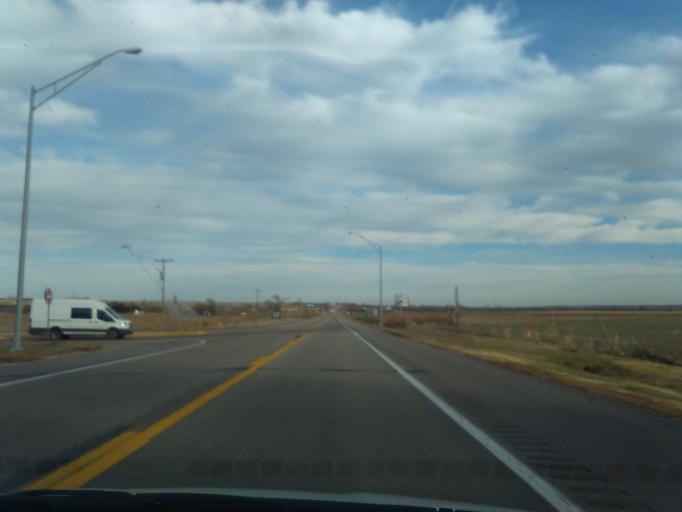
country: US
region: Nebraska
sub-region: Hitchcock County
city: Trenton
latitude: 40.2343
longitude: -100.8956
